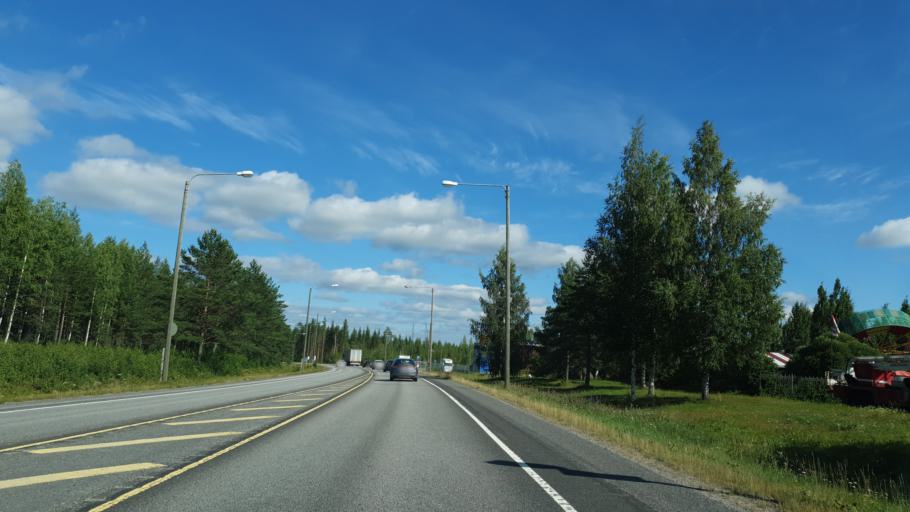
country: FI
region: Central Finland
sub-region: Jyvaeskylae
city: Toivakka
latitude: 62.2464
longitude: 26.1377
